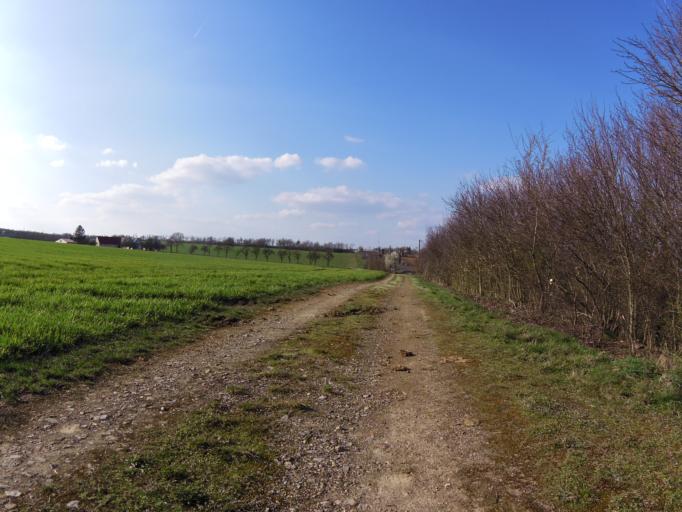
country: DE
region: Bavaria
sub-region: Regierungsbezirk Unterfranken
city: Biebelried
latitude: 49.7825
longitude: 10.0970
